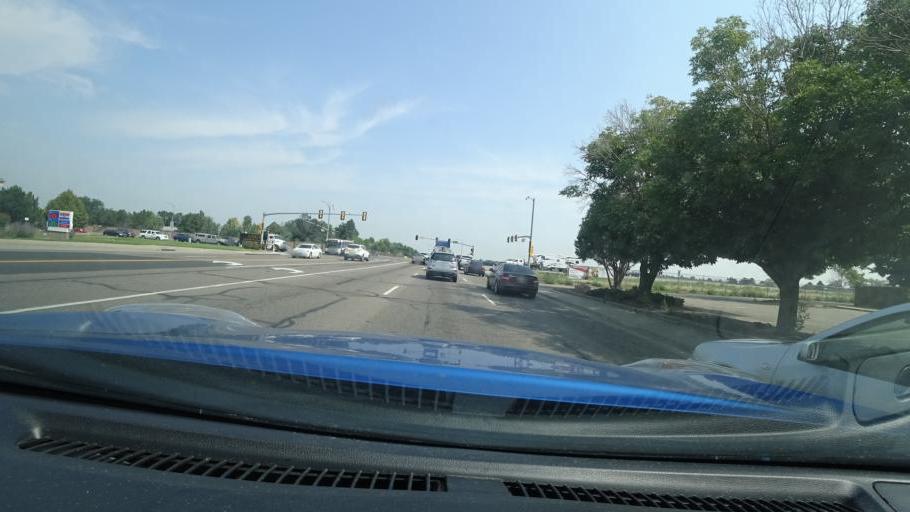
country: US
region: Colorado
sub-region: Adams County
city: Aurora
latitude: 39.7250
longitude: -104.7910
